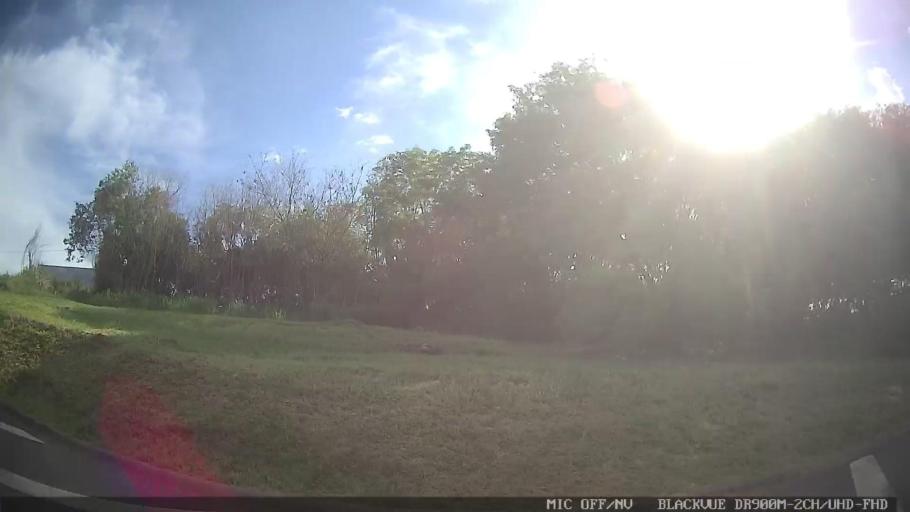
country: BR
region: Sao Paulo
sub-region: Laranjal Paulista
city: Laranjal Paulista
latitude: -23.0662
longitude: -47.8187
